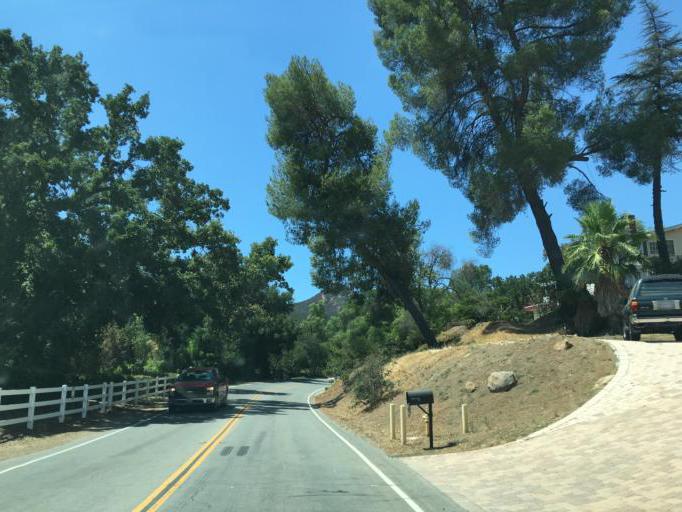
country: US
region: California
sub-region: Los Angeles County
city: Agoura Hills
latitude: 34.1074
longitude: -118.7627
